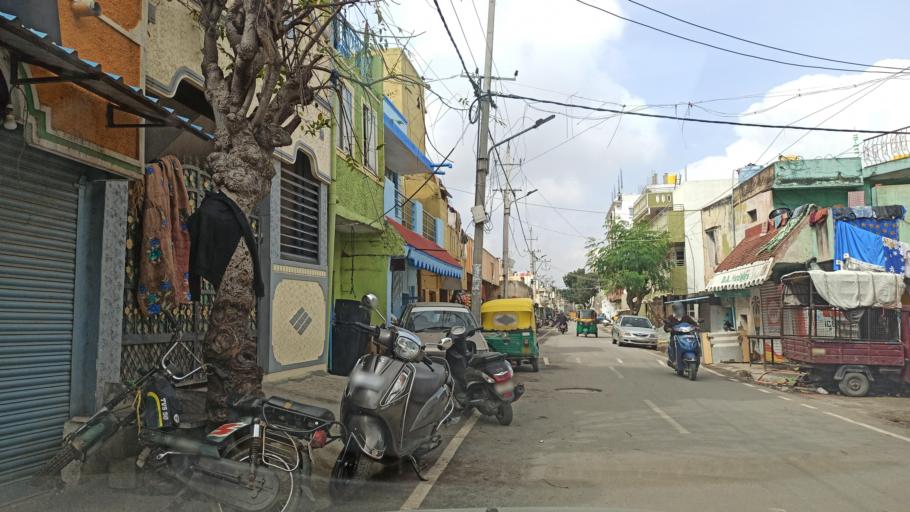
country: IN
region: Karnataka
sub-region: Bangalore Urban
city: Bangalore
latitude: 13.0019
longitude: 77.6720
